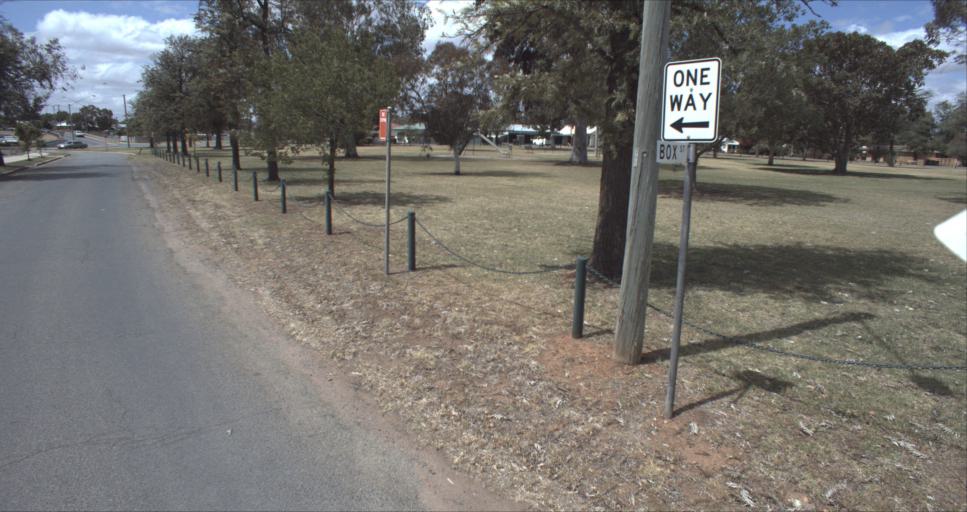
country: AU
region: New South Wales
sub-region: Leeton
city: Leeton
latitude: -34.5576
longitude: 146.3988
